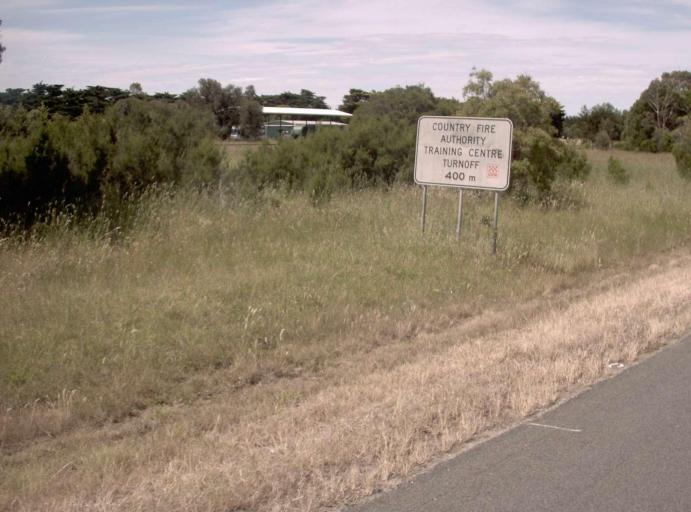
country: AU
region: Victoria
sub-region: Wellington
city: Sale
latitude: -38.1011
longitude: 146.9541
